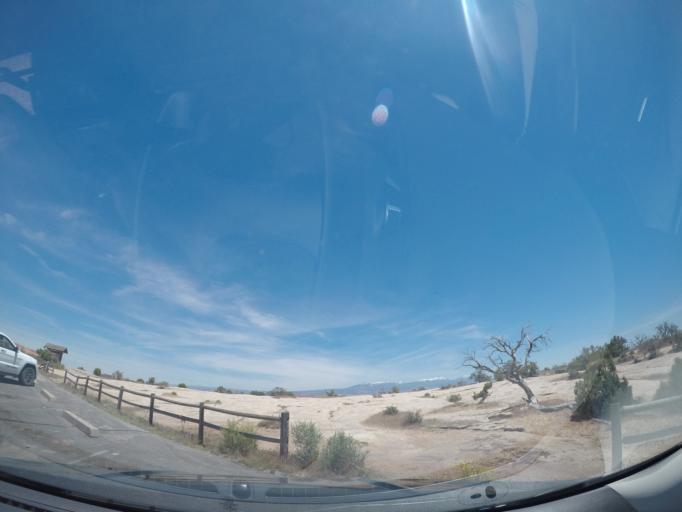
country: US
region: Utah
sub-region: Grand County
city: Moab
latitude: 38.6297
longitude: -109.7998
